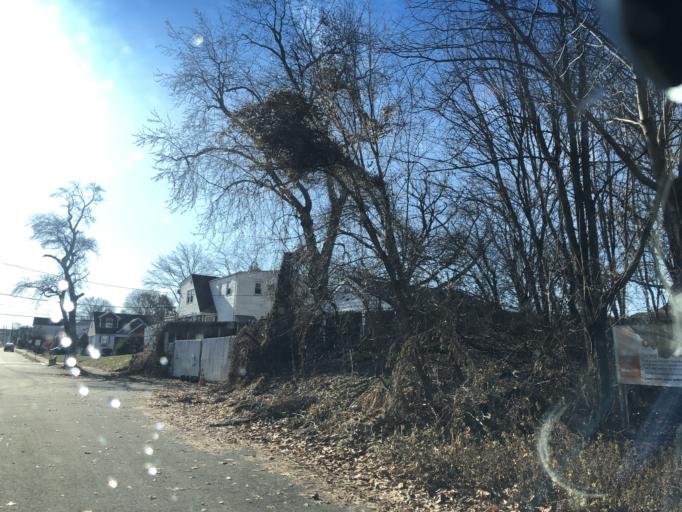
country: US
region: New Jersey
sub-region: Bergen County
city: Fair Lawn
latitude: 40.9267
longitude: -74.1435
